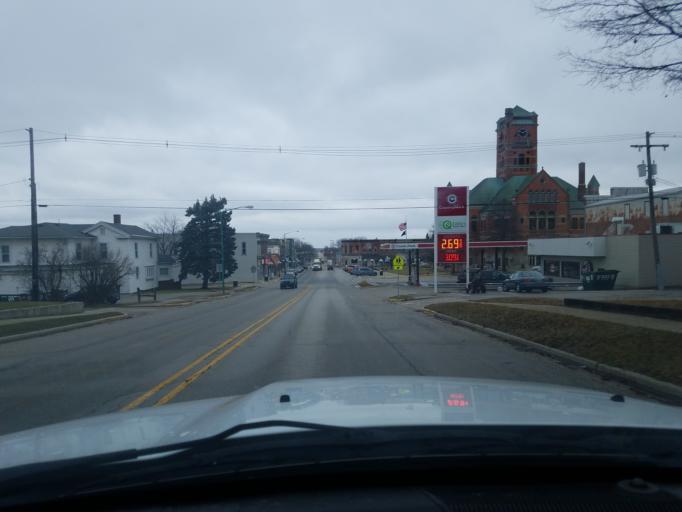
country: US
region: Indiana
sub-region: Noble County
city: Albion
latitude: 41.3973
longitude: -85.4241
